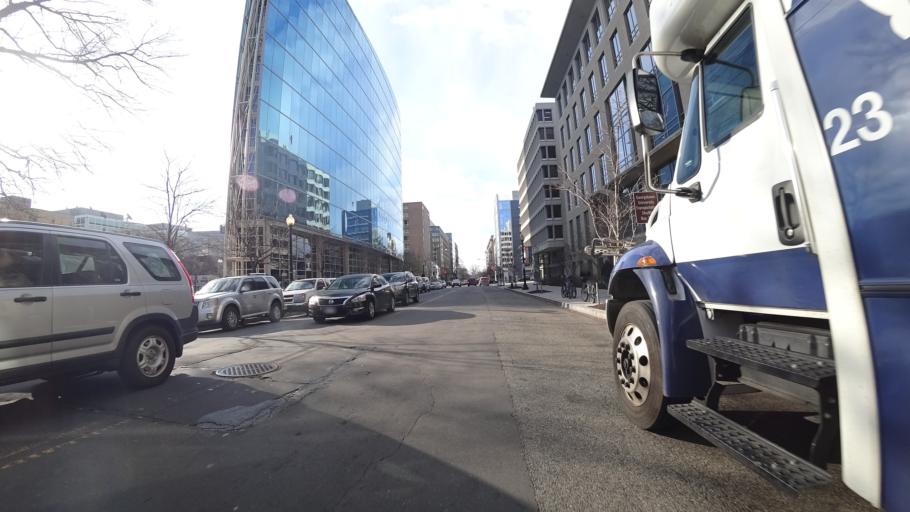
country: US
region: Washington, D.C.
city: Washington, D.C.
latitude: 38.8970
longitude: -77.0122
